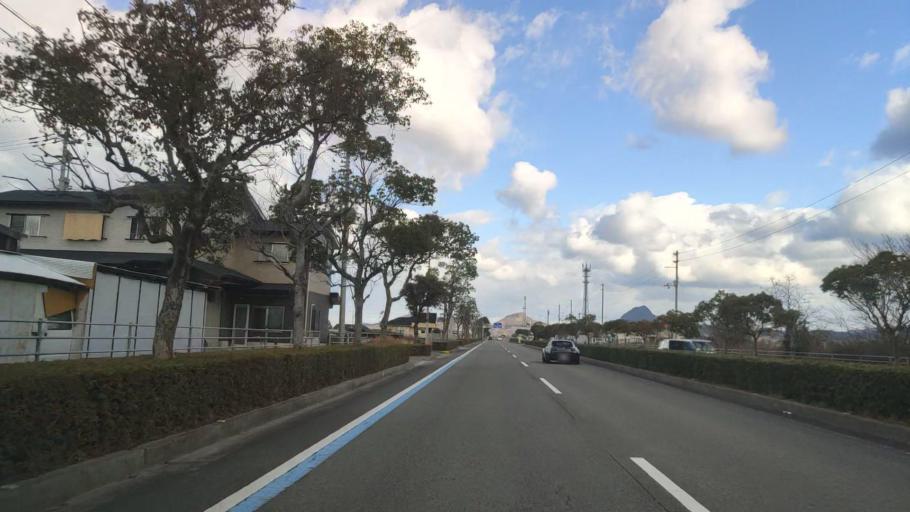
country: JP
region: Ehime
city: Hojo
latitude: 33.9509
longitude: 132.7744
